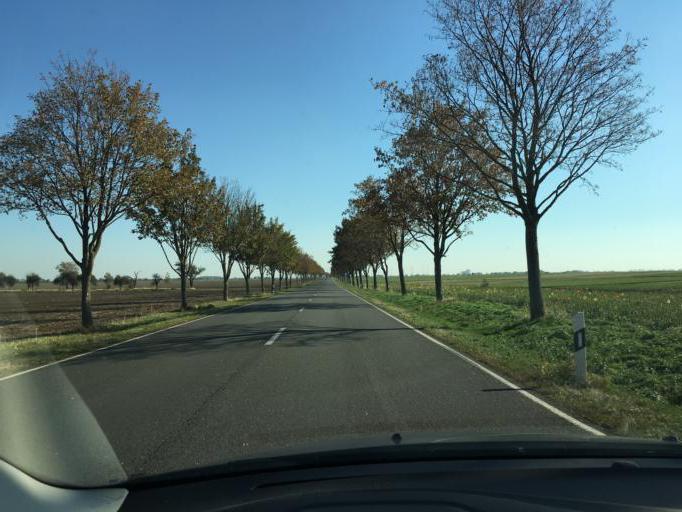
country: DE
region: Saxony-Anhalt
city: Wanzleben
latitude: 52.0243
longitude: 11.4914
